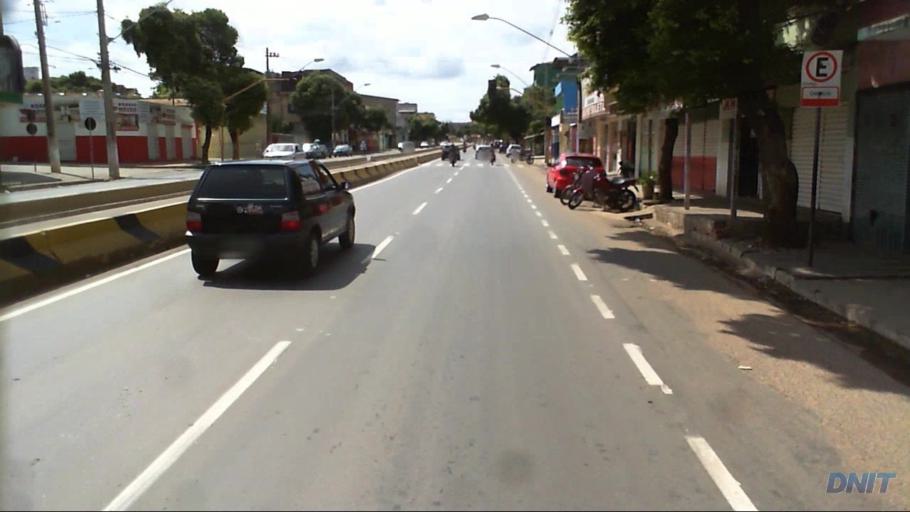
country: BR
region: Minas Gerais
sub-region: Governador Valadares
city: Governador Valadares
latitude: -18.8822
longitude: -41.9654
